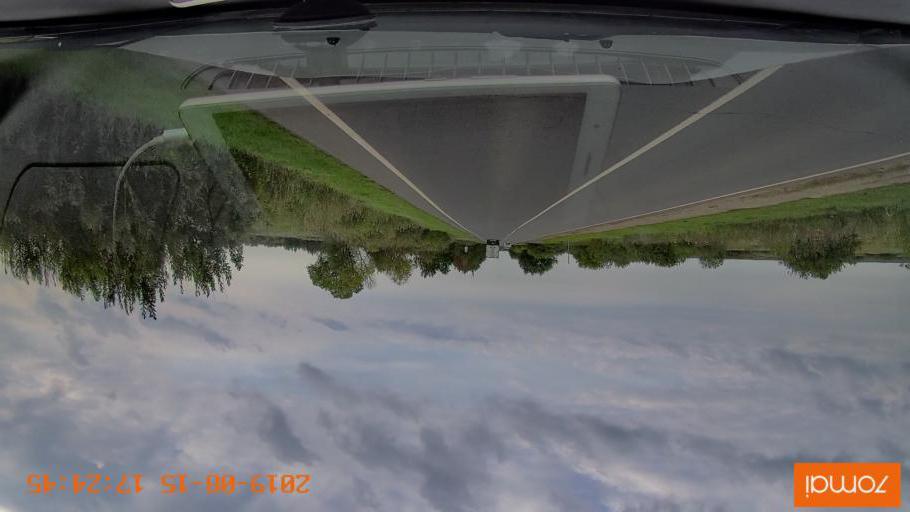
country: RU
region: Moskovskaya
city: Ashitkovo
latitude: 55.3830
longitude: 38.5577
